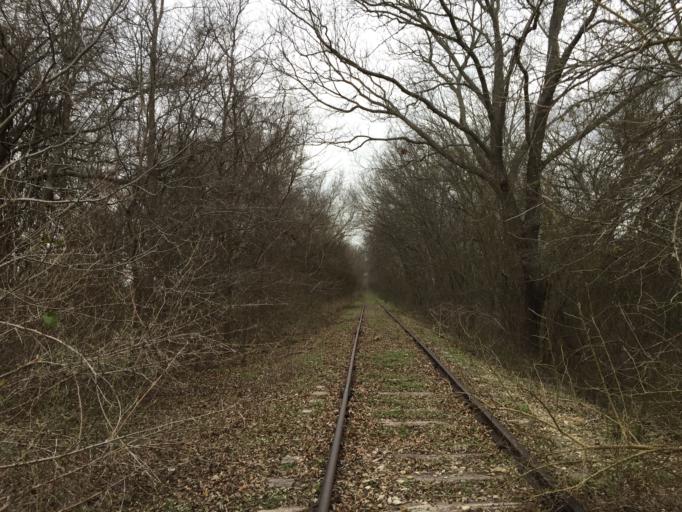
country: US
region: Texas
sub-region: Bell County
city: Belton
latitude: 31.0454
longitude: -97.4206
